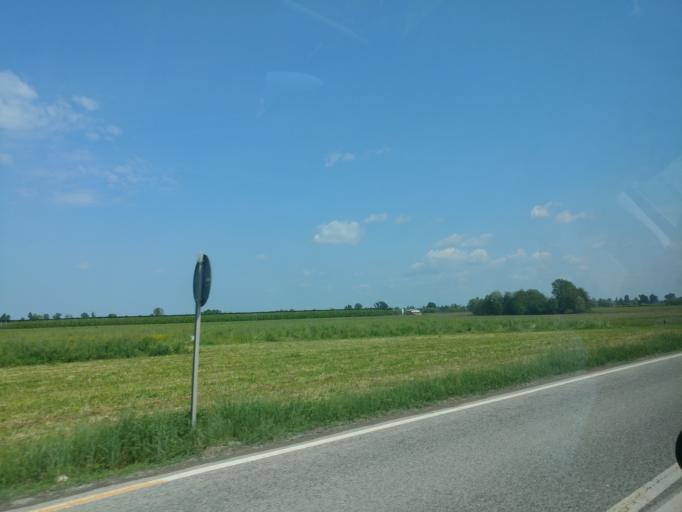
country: IT
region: Piedmont
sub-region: Provincia di Cuneo
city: Carde
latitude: 44.7324
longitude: 7.4245
